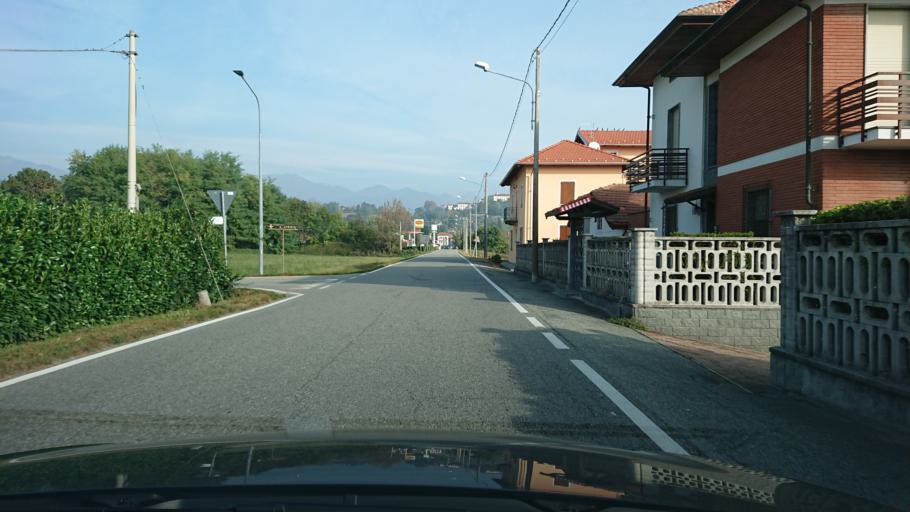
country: IT
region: Piedmont
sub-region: Provincia di Biella
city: Valdengo
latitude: 45.5650
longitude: 8.1315
